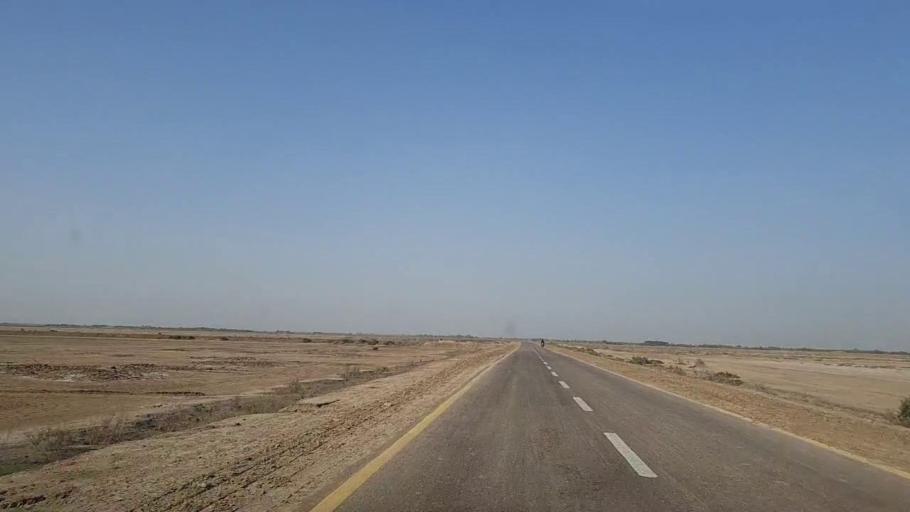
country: PK
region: Sindh
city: Jati
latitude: 24.4956
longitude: 68.3763
